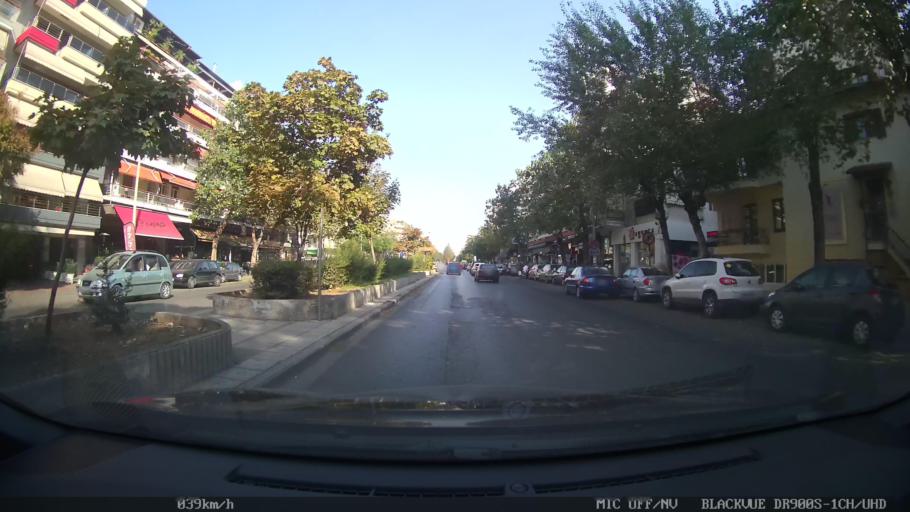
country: GR
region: Central Macedonia
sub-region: Nomos Thessalonikis
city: Triandria
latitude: 40.6008
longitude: 22.9644
